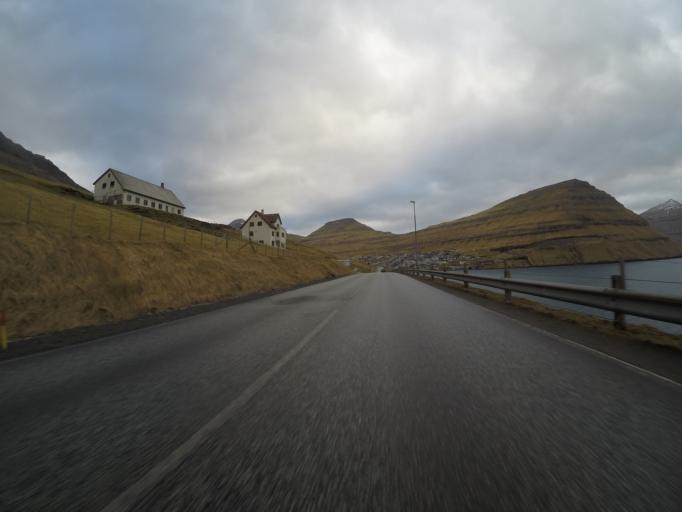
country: FO
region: Nordoyar
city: Klaksvik
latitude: 62.2440
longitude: -6.5891
